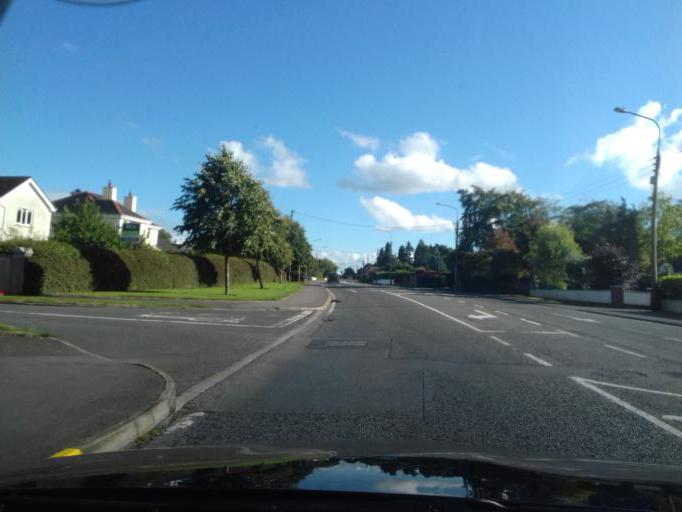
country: IE
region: Leinster
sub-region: Uibh Fhaili
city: Tullamore
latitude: 53.2596
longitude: -7.4844
